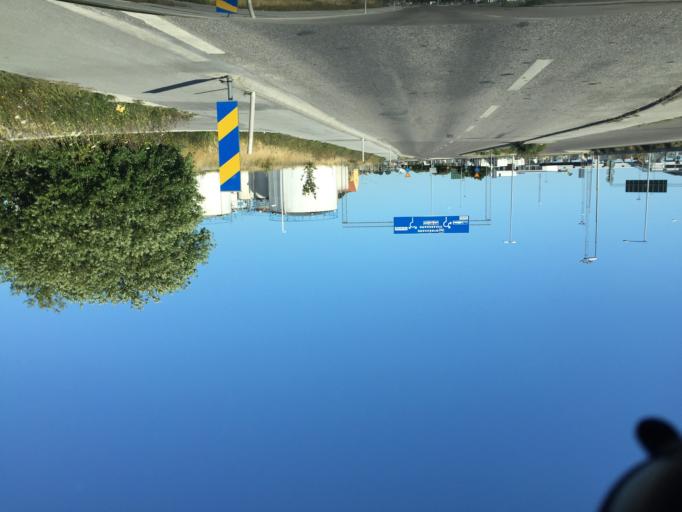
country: SE
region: Gotland
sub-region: Gotland
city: Visby
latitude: 57.6304
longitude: 18.2766
